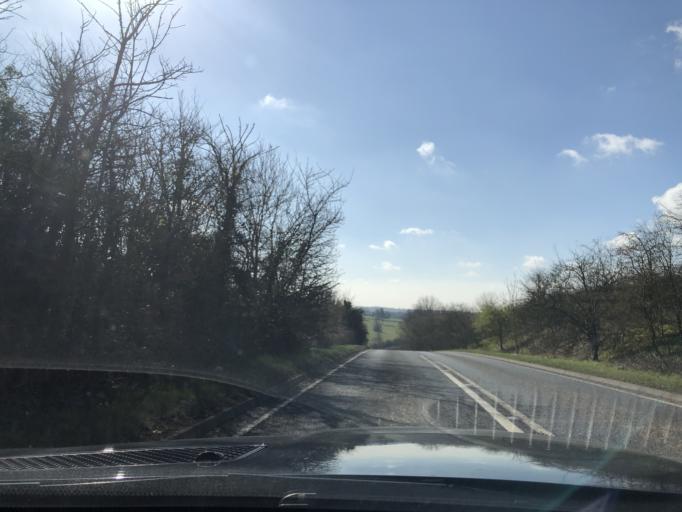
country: GB
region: England
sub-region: Warwickshire
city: Ryton on Dunsmore
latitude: 52.3293
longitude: -1.4158
